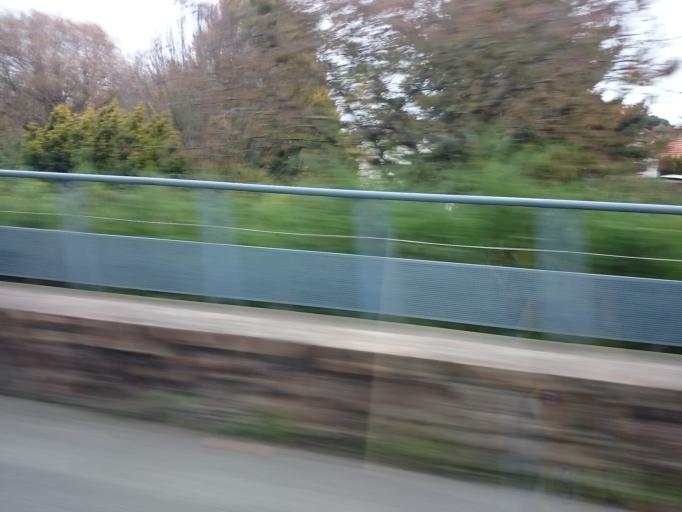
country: FR
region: Pays de la Loire
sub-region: Departement de la Loire-Atlantique
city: Indre
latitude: 47.1996
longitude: -1.6701
